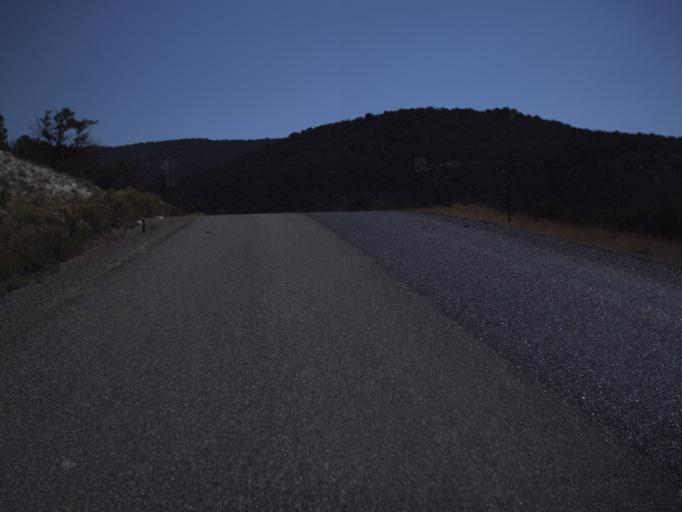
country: US
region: Utah
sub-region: Sevier County
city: Salina
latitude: 38.8800
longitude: -111.5631
